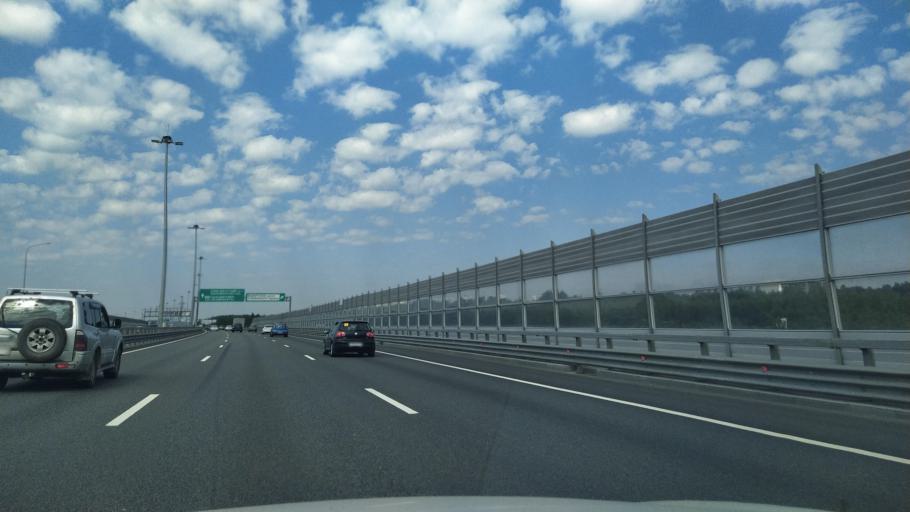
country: RU
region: St.-Petersburg
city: Pargolovo
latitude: 60.0983
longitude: 30.2982
